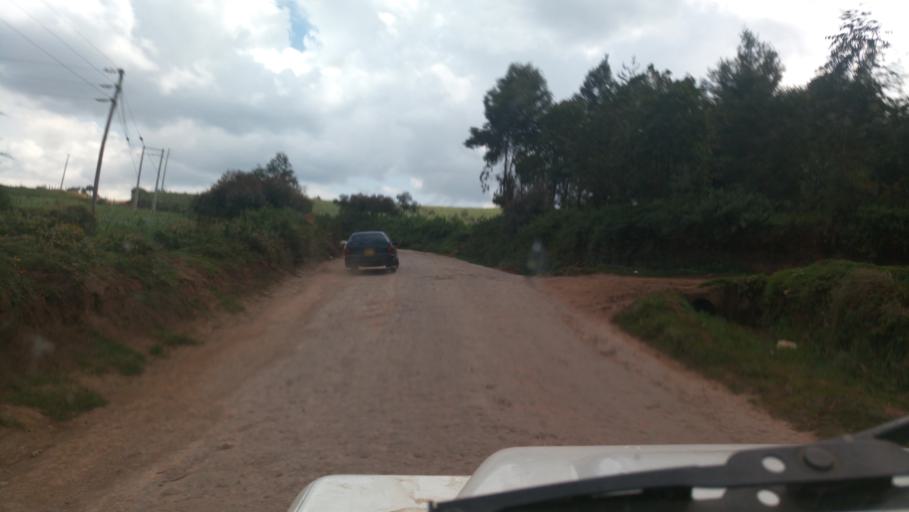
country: KE
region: Nakuru
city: Molo
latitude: -0.2978
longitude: 35.6853
